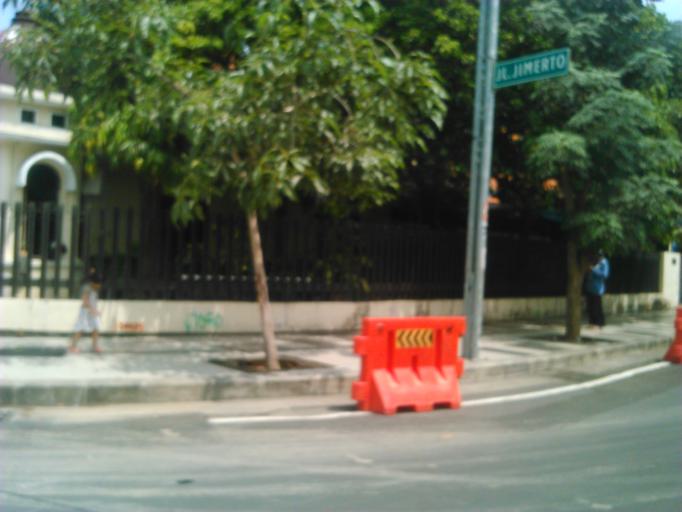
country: ID
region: East Java
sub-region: Kota Surabaya
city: Surabaya
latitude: -7.2581
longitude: 112.7480
